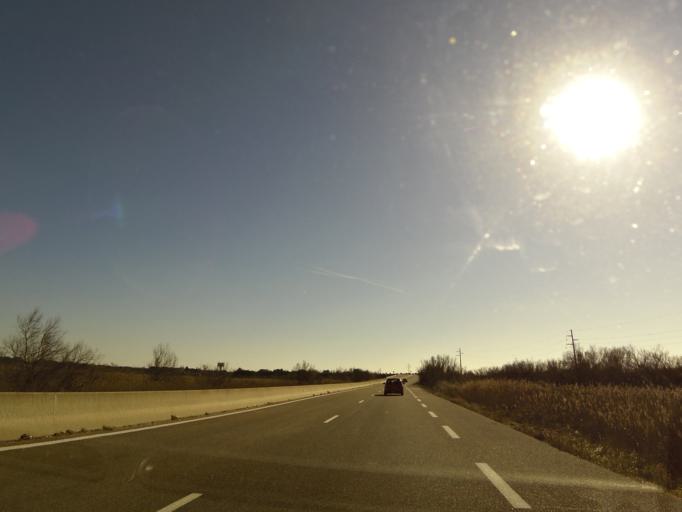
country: FR
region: Languedoc-Roussillon
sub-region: Departement du Gard
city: Aigues-Mortes
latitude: 43.5935
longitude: 4.1960
